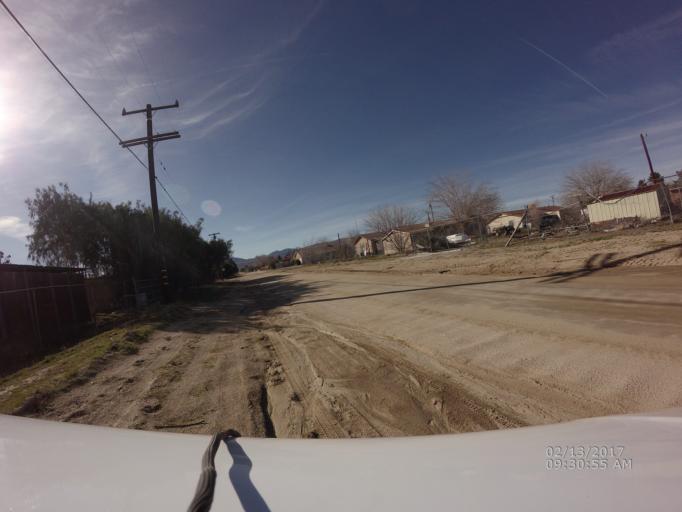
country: US
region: California
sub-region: Los Angeles County
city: Littlerock
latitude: 34.5400
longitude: -117.9625
